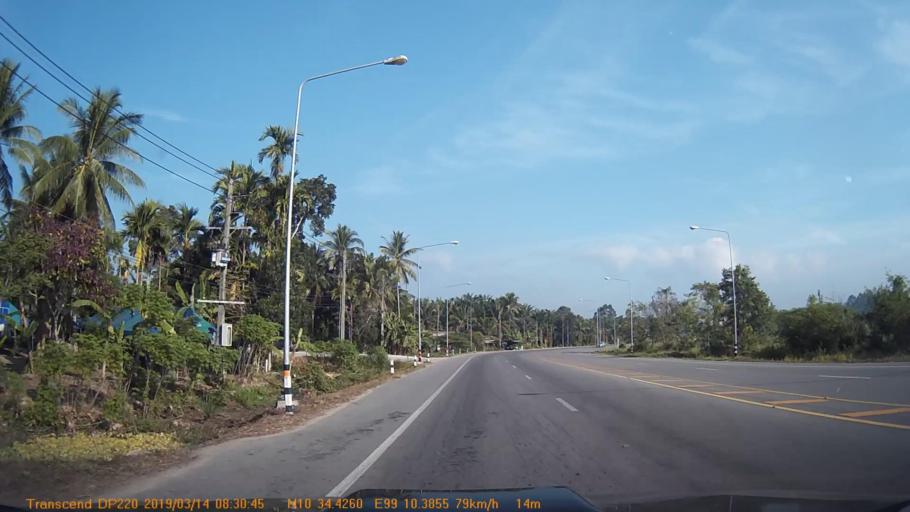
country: TH
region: Chumphon
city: Chumphon
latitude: 10.5739
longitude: 99.1730
